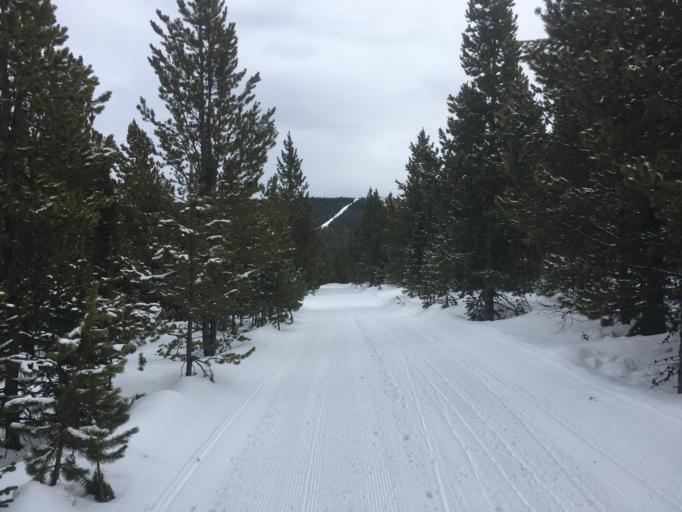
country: US
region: Montana
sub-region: Meagher County
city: White Sulphur Springs
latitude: 46.8487
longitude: -110.7090
